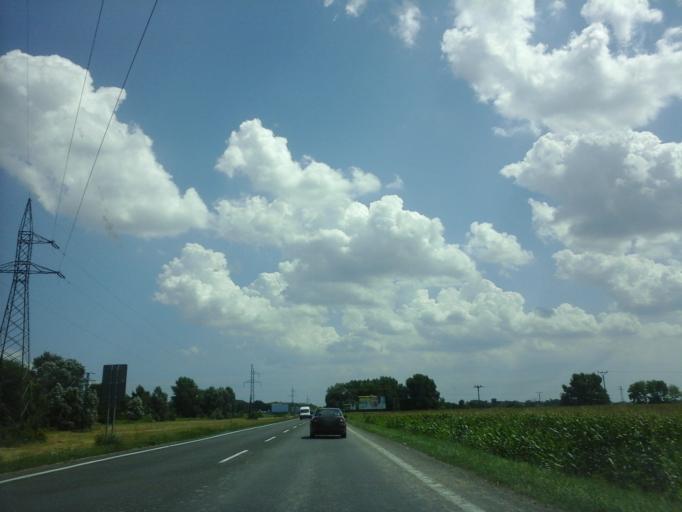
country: AT
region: Burgenland
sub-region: Politischer Bezirk Neusiedl am See
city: Kittsee
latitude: 48.0785
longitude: 17.1296
